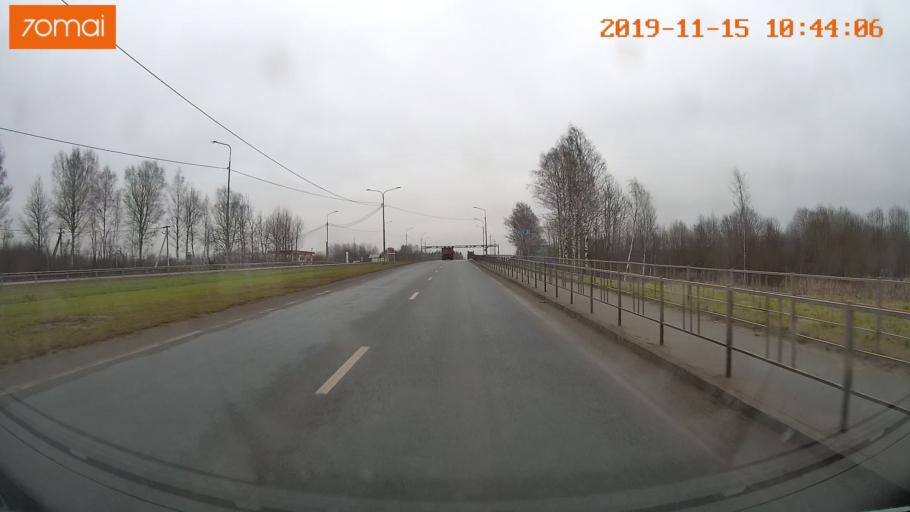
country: RU
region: Vologda
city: Sheksna
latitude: 59.2115
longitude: 38.5504
